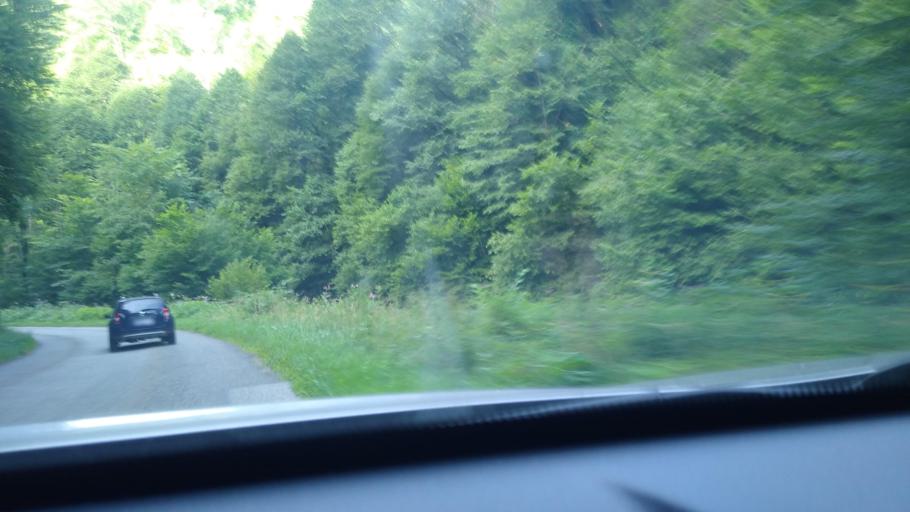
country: FR
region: Midi-Pyrenees
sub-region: Departement de l'Ariege
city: Saint-Girons
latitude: 42.8204
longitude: 1.1965
